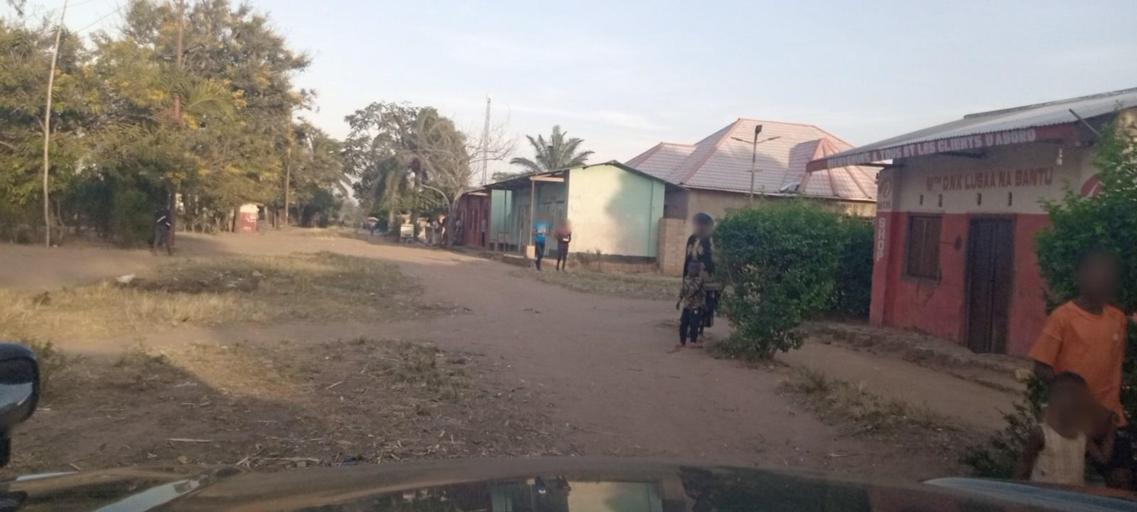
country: CD
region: Kasai-Oriental
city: Lubao
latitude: -5.3848
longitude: 25.7450
